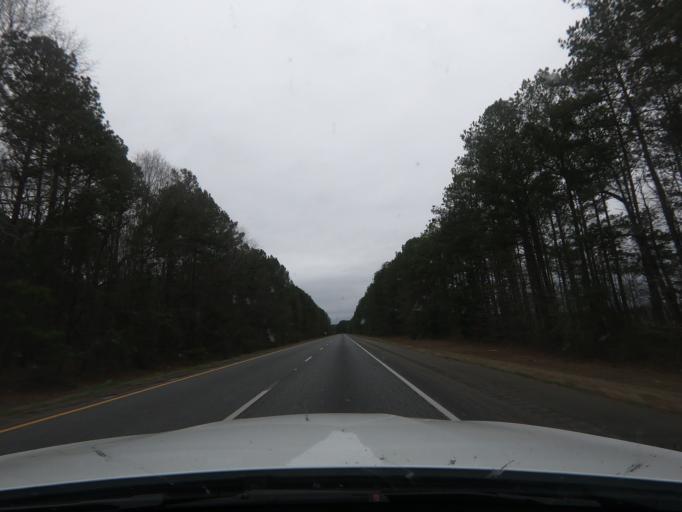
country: US
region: Georgia
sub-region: Troup County
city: La Grange
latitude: 32.9787
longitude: -84.9514
